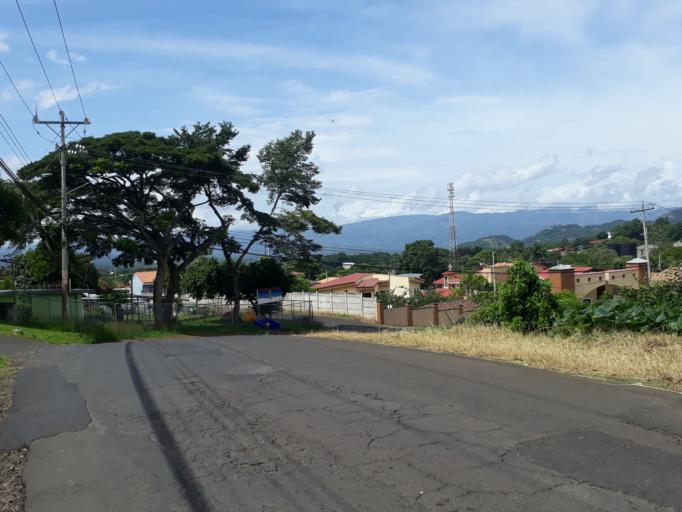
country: CR
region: Alajuela
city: Atenas
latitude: 10.0201
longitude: -84.3410
